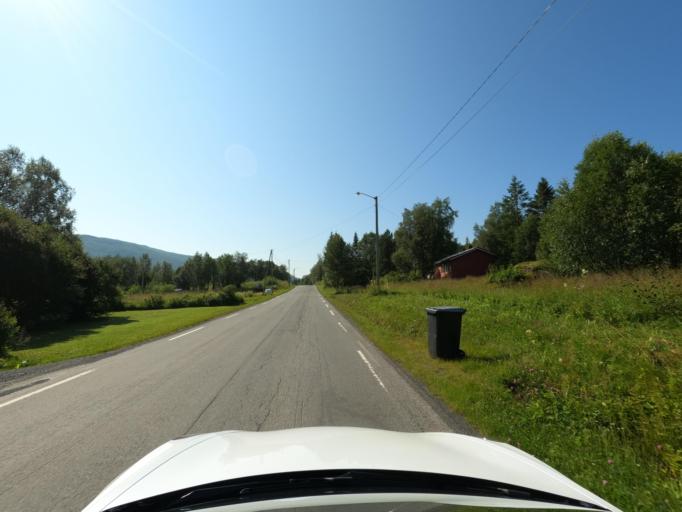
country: NO
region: Nordland
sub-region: Ballangen
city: Ballangen
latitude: 68.3537
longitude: 16.8641
